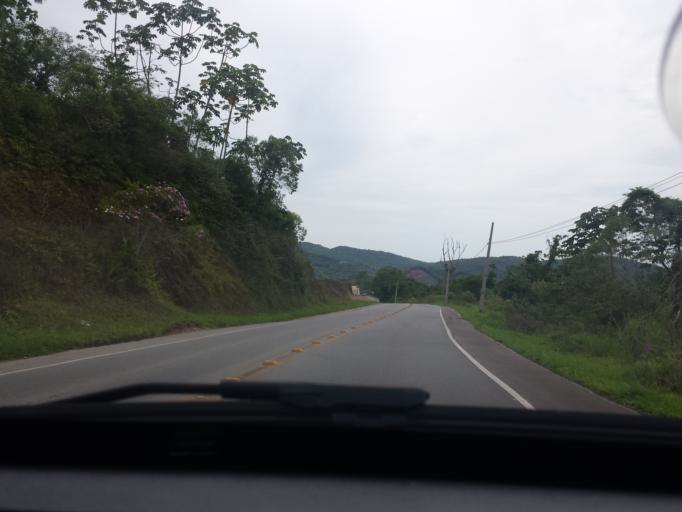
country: BR
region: Santa Catarina
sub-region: Blumenau
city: Blumenau
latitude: -26.8926
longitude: -49.0114
